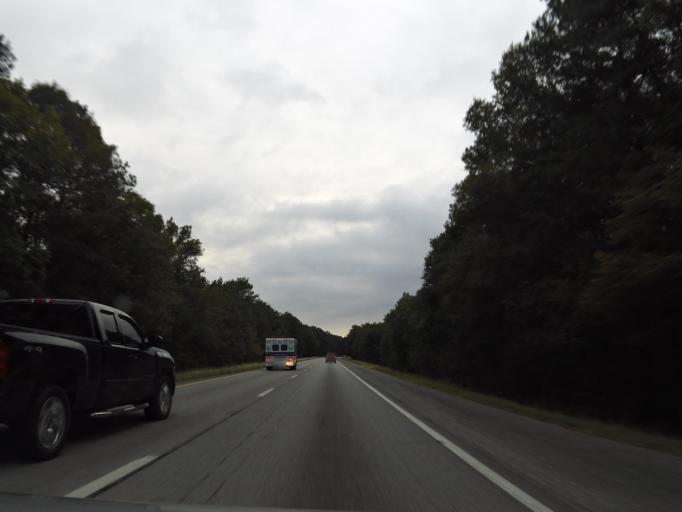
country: US
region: Alabama
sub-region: Saint Clair County
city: Springville
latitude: 33.7915
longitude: -86.3857
